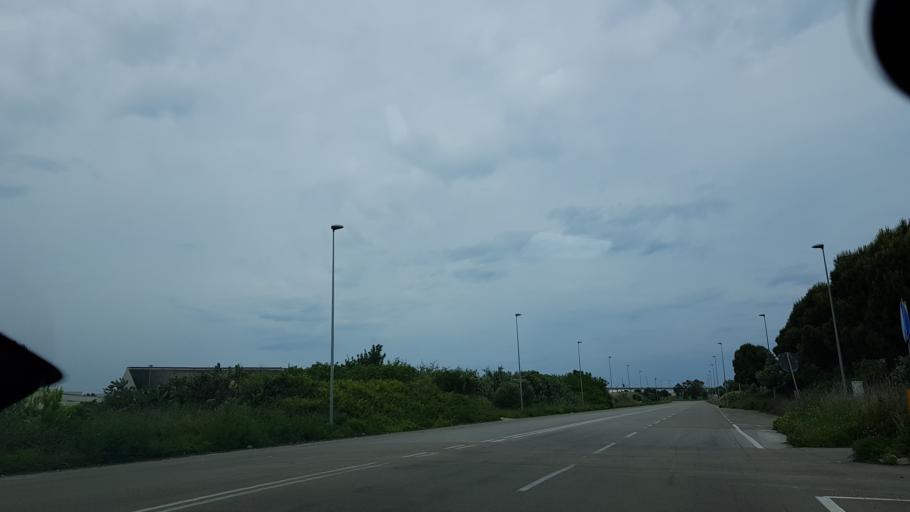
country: IT
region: Apulia
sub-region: Provincia di Brindisi
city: Materdomini
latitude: 40.6368
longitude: 17.9670
